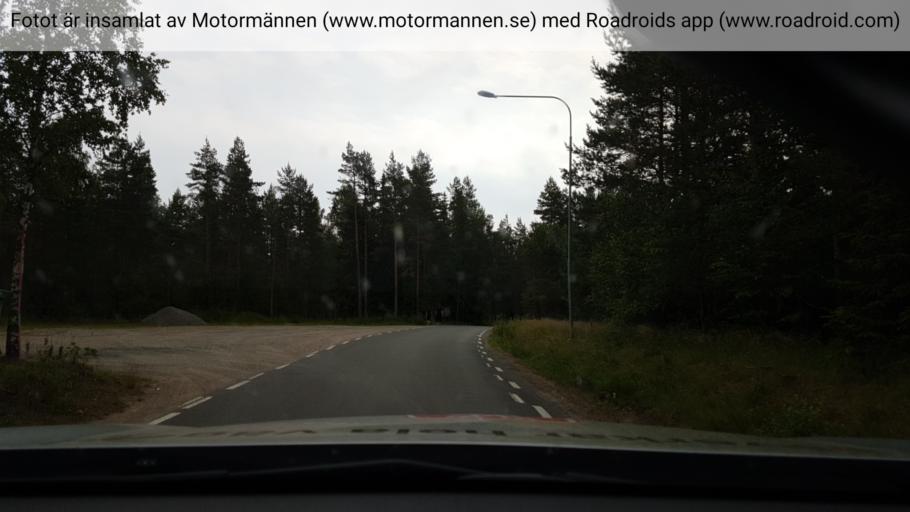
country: SE
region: Vaestra Goetaland
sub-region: Tidaholms Kommun
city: Tidaholm
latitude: 58.0795
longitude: 14.0692
